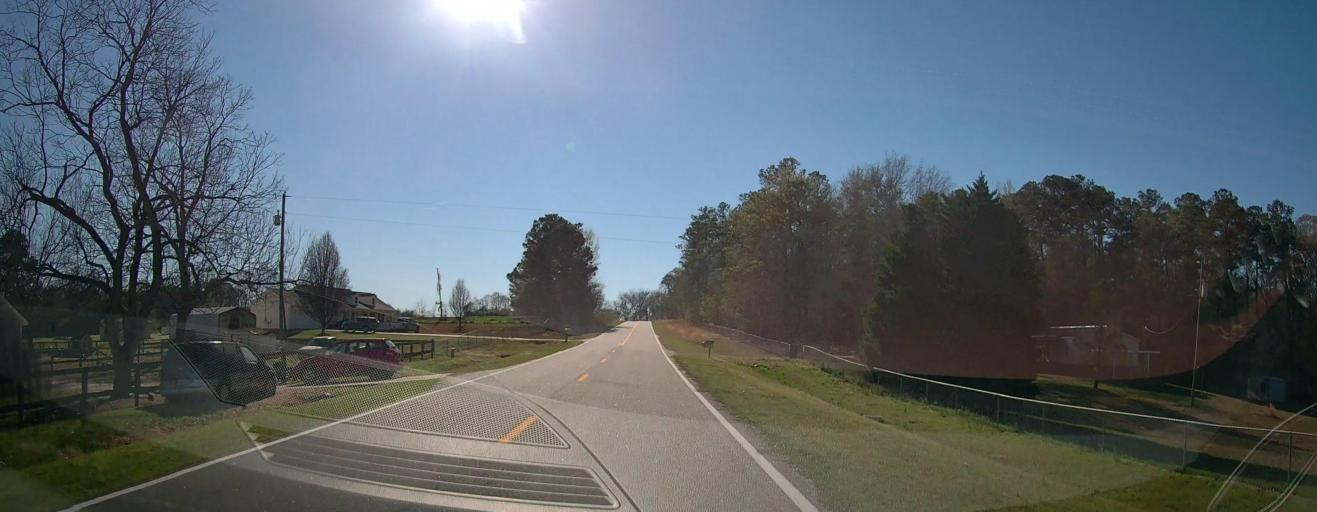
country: US
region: Georgia
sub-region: Peach County
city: Byron
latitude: 32.6755
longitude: -83.8149
